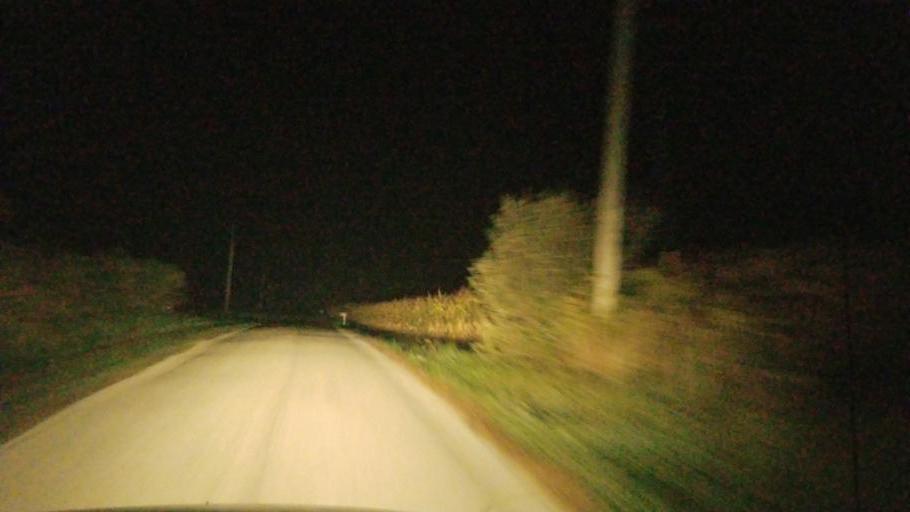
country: US
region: Ohio
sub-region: Highland County
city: Leesburg
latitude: 39.3014
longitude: -83.5618
